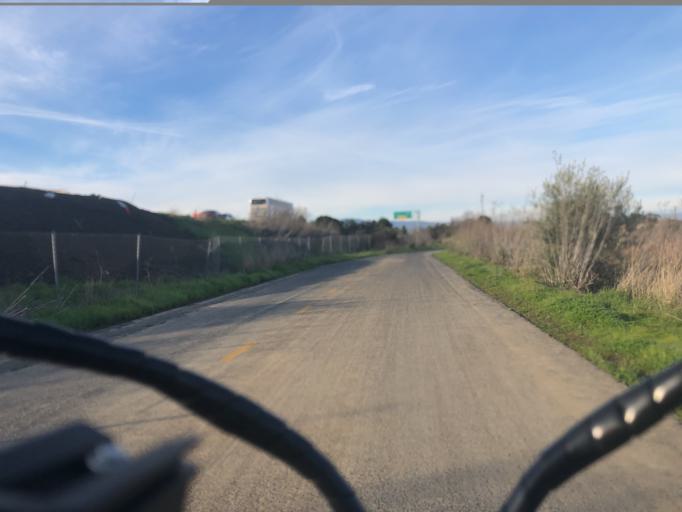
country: US
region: California
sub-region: Santa Clara County
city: Santa Clara
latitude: 37.4131
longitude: -121.9850
